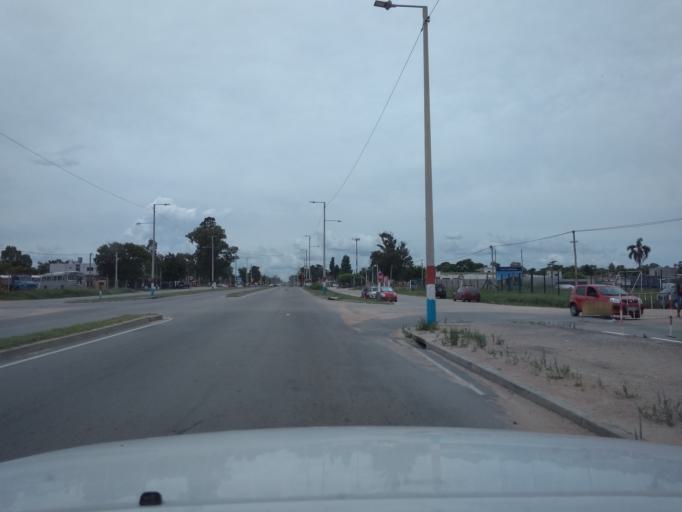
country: UY
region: Canelones
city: Paso de Carrasco
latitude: -34.8630
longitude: -56.0555
